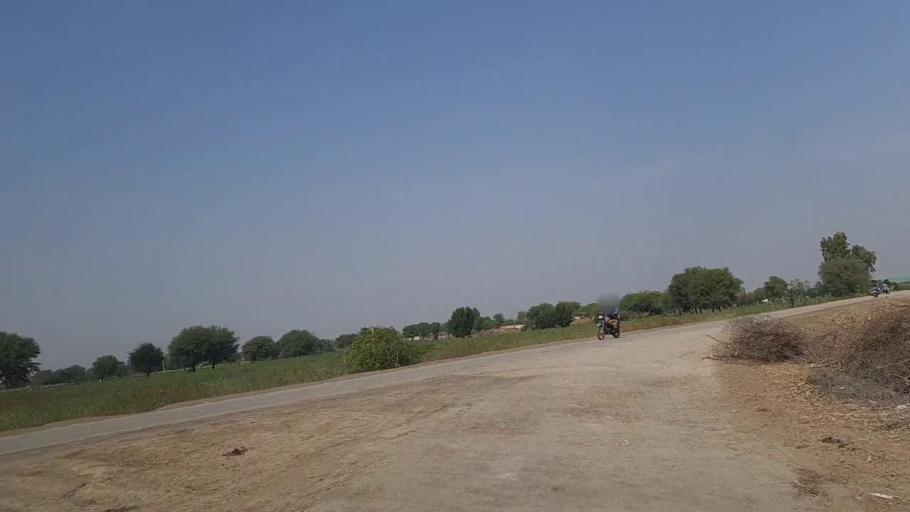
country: PK
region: Sindh
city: Samaro
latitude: 25.2692
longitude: 69.3929
